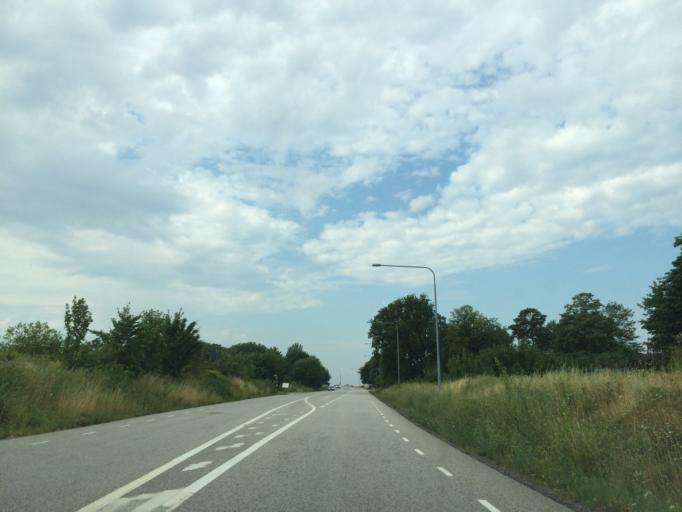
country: SE
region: Skane
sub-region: Malmo
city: Oxie
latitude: 55.5859
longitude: 13.1021
